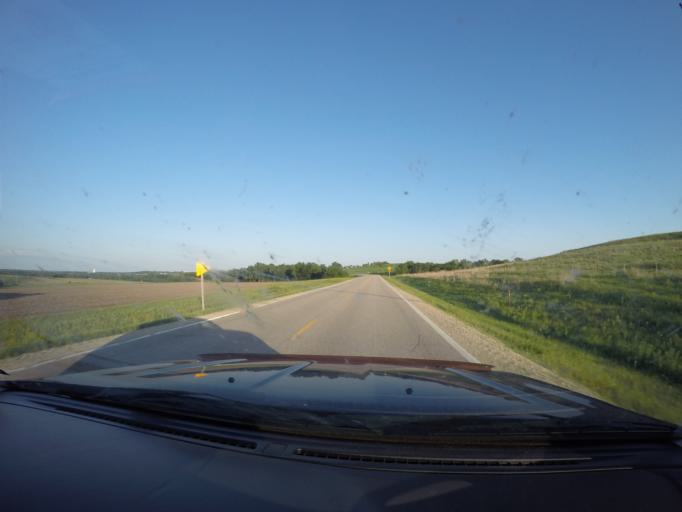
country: US
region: Kansas
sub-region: Marshall County
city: Blue Rapids
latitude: 39.6928
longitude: -96.7880
